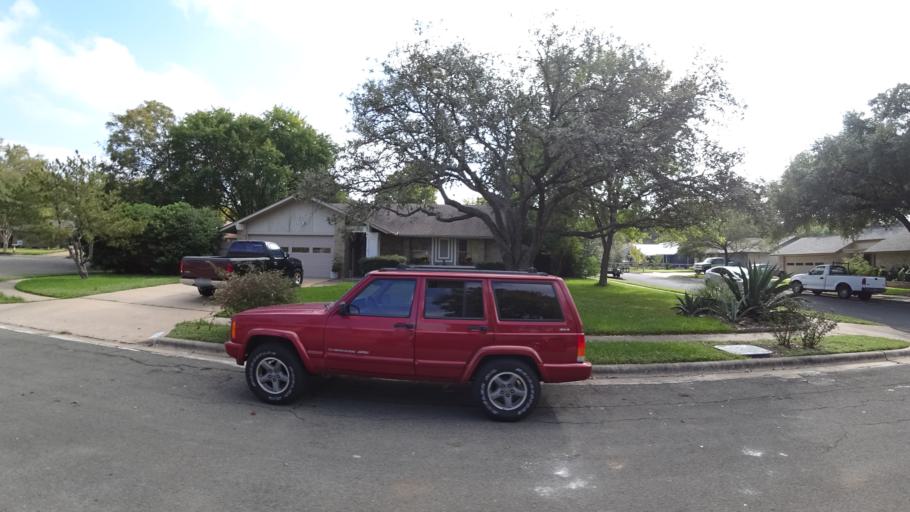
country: US
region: Texas
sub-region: Travis County
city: Shady Hollow
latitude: 30.2045
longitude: -97.8144
